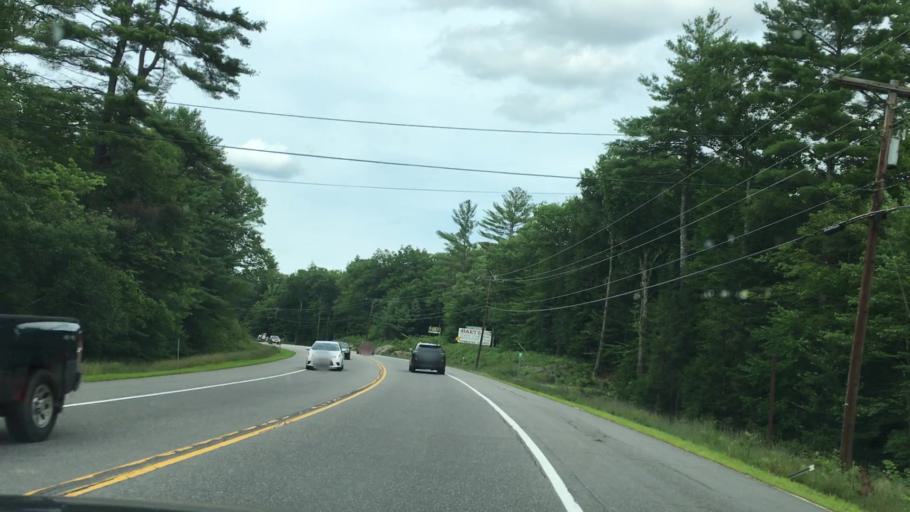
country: US
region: New Hampshire
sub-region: Belknap County
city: Meredith
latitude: 43.6294
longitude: -71.5327
